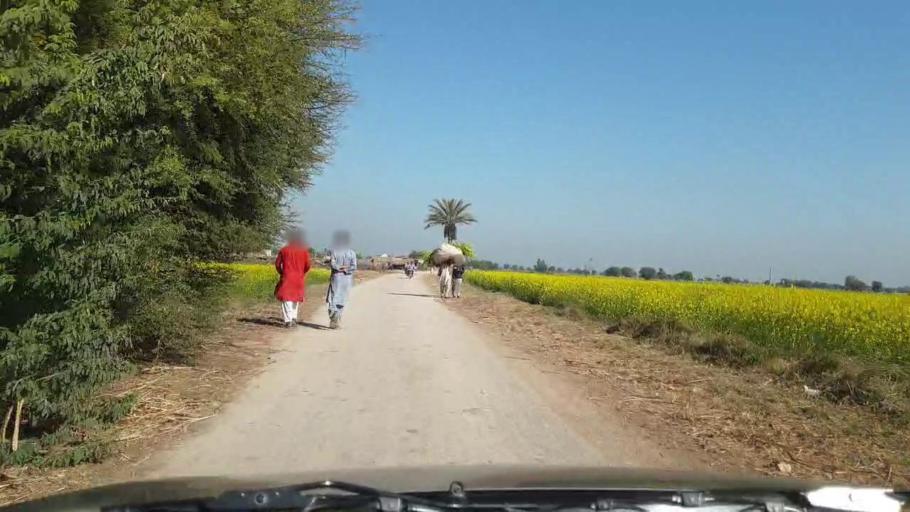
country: PK
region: Sindh
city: Jhol
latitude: 25.9483
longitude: 68.8196
